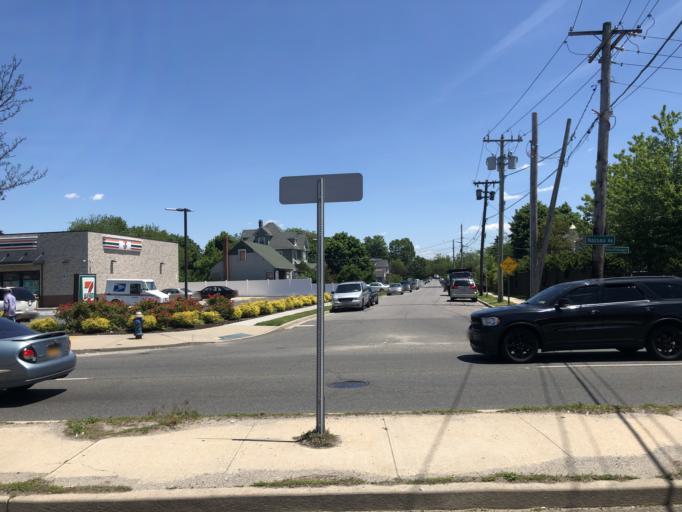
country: US
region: New York
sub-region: Nassau County
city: Roosevelt
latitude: 40.6826
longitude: -73.5918
